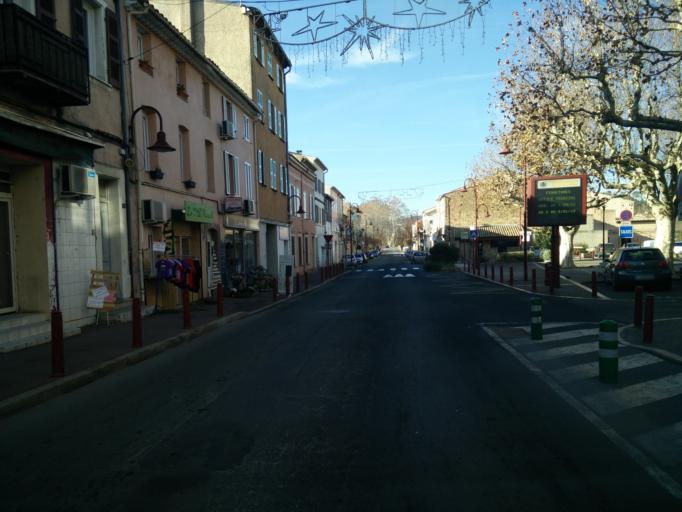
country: FR
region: Provence-Alpes-Cote d'Azur
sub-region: Departement du Var
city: Vidauban
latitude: 43.4274
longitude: 6.4310
